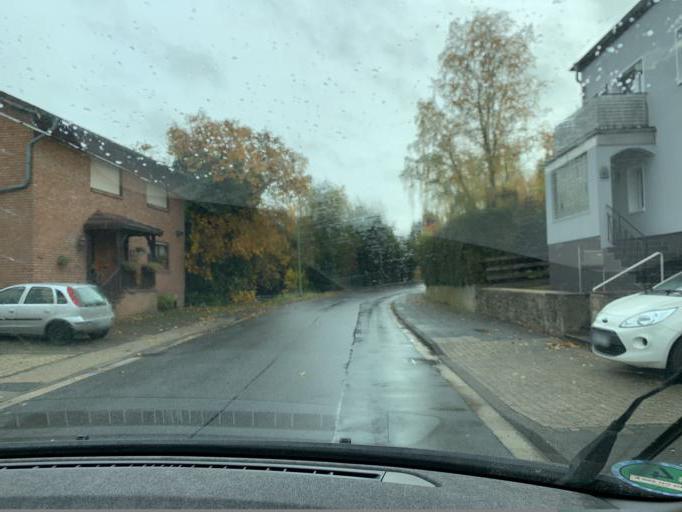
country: DE
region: North Rhine-Westphalia
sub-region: Regierungsbezirk Koln
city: Nideggen
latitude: 50.7156
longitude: 6.4669
